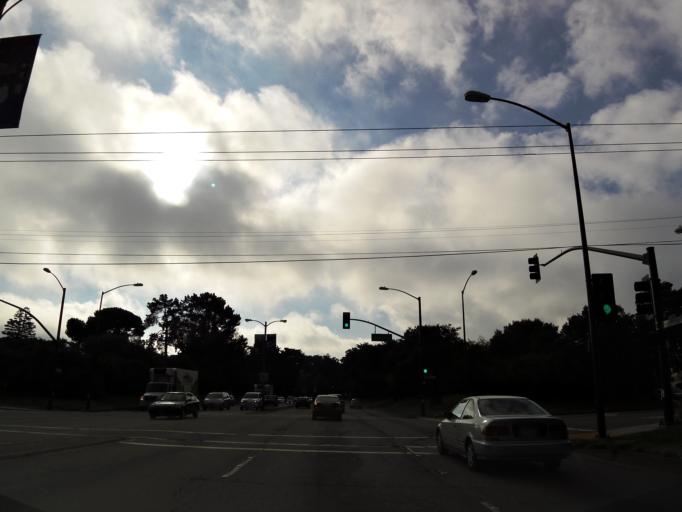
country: US
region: California
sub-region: San Francisco County
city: San Francisco
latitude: 37.7753
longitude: -122.4721
